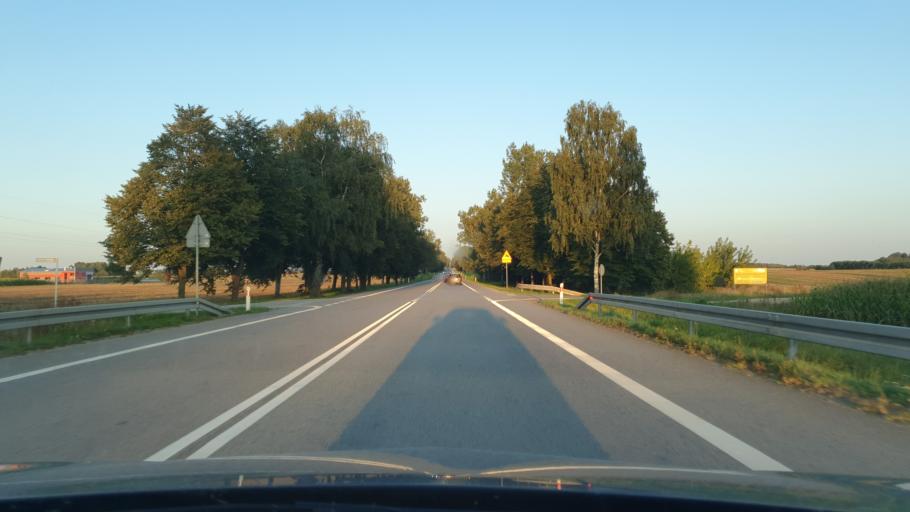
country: PL
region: Pomeranian Voivodeship
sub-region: Powiat slupski
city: Potegowo
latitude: 54.4768
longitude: 17.5018
